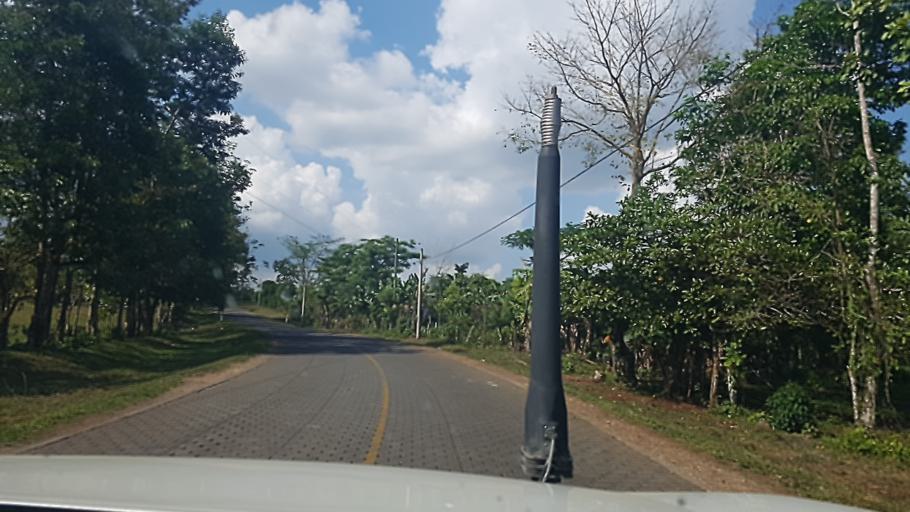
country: NI
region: Atlantico Sur
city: Nueva Guinea
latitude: 11.6981
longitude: -84.3860
